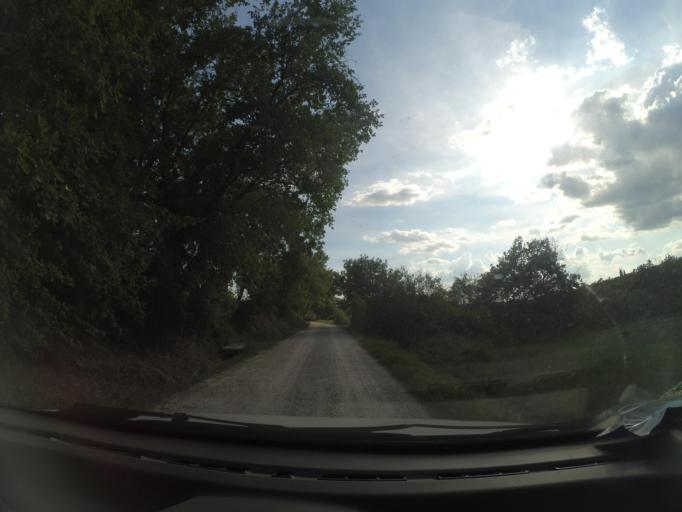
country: IT
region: Tuscany
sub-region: Province of Arezzo
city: Castiglion Fibocchi
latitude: 43.5369
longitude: 11.7666
